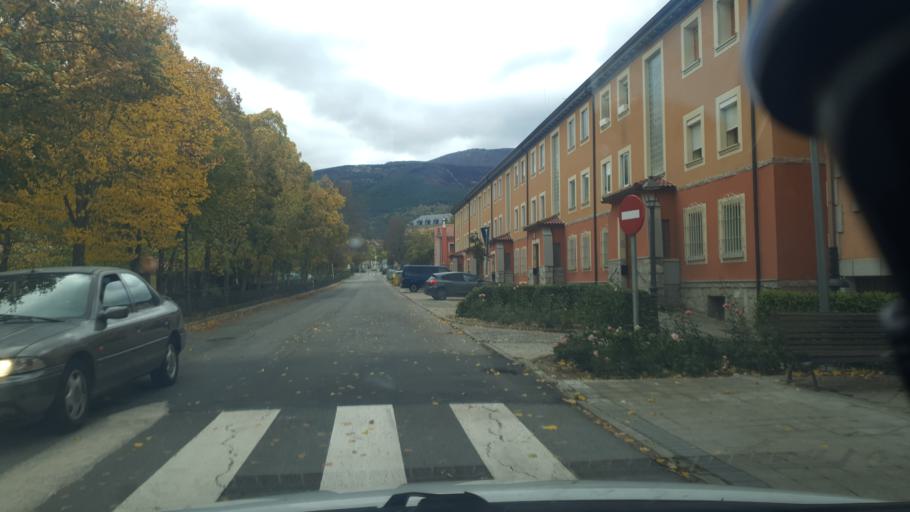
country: ES
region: Castille and Leon
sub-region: Provincia de Segovia
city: San Ildefonso
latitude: 40.9019
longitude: -4.0112
